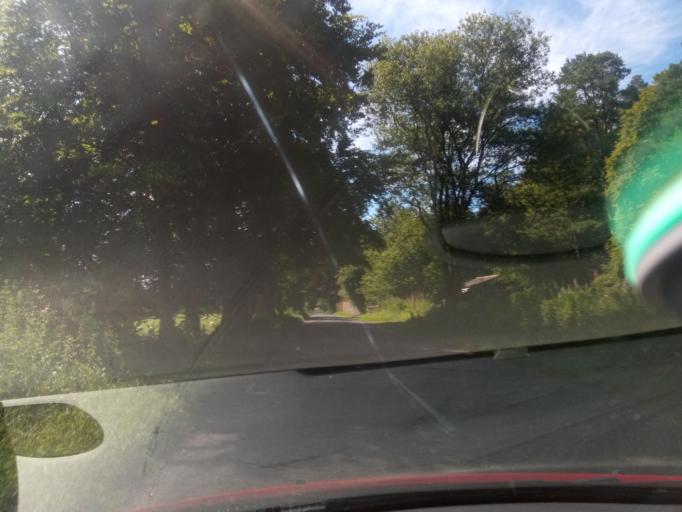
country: GB
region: England
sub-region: Northumberland
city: Bardon Mill
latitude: 54.9168
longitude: -2.3349
